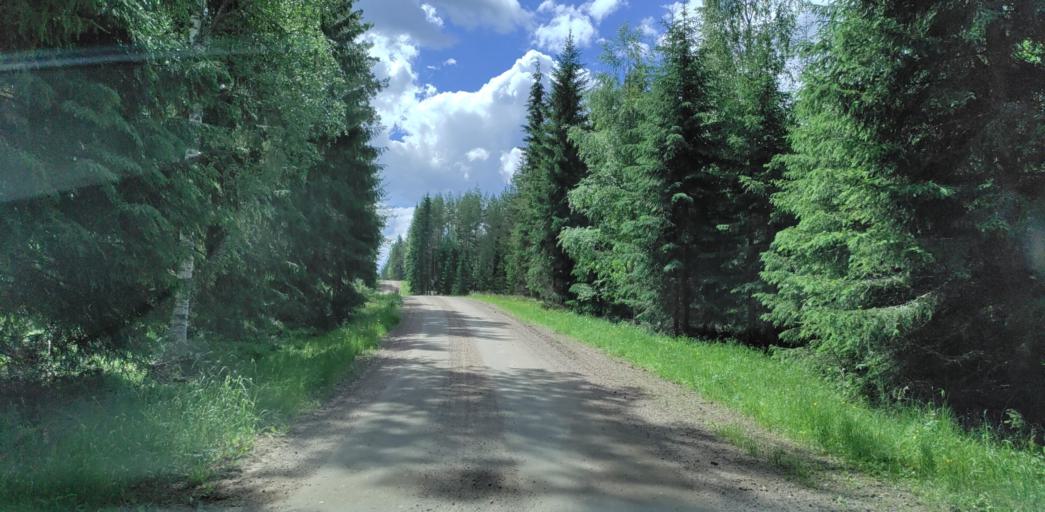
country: SE
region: Vaermland
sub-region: Hagfors Kommun
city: Ekshaerad
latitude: 60.1009
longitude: 13.3518
